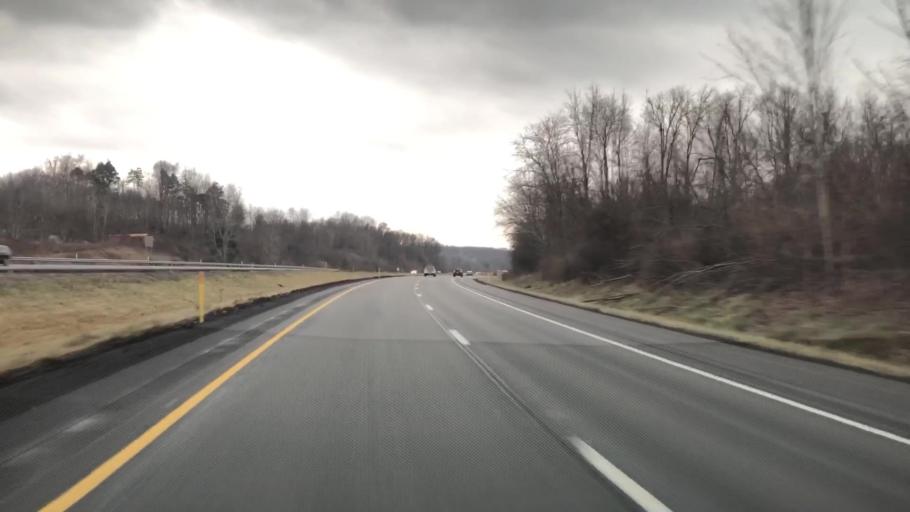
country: US
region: Pennsylvania
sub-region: Butler County
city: Prospect
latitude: 40.9693
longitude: -80.1330
